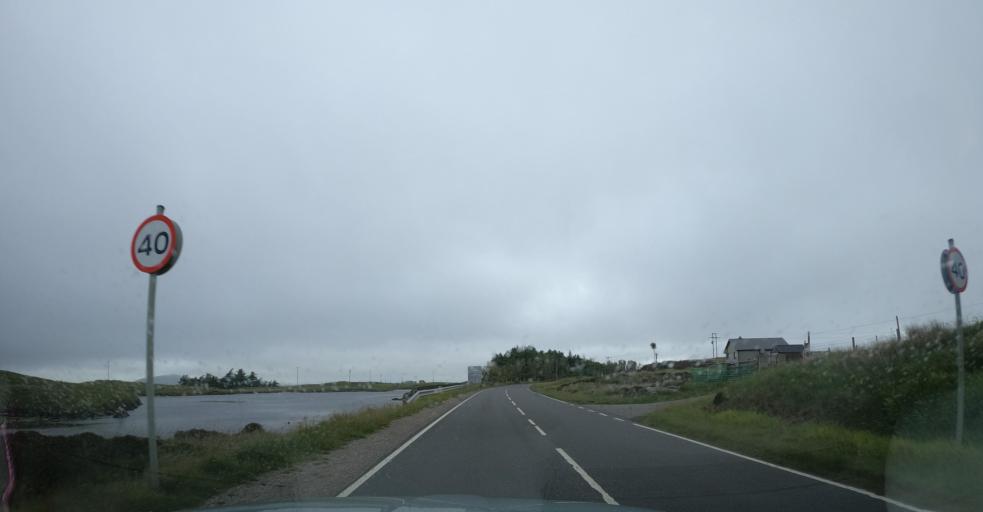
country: GB
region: Scotland
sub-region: Eilean Siar
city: Isle of North Uist
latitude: 57.6053
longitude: -7.1774
